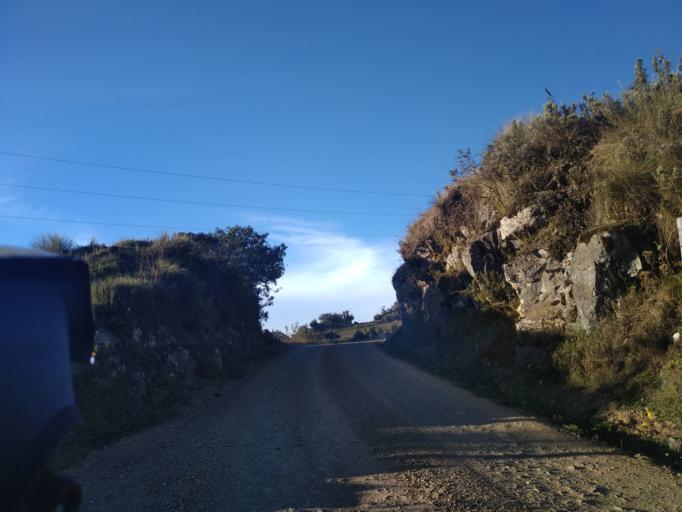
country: PE
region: Amazonas
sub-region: Provincia de Chachapoyas
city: Montevideo
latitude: -6.7156
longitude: -77.8661
